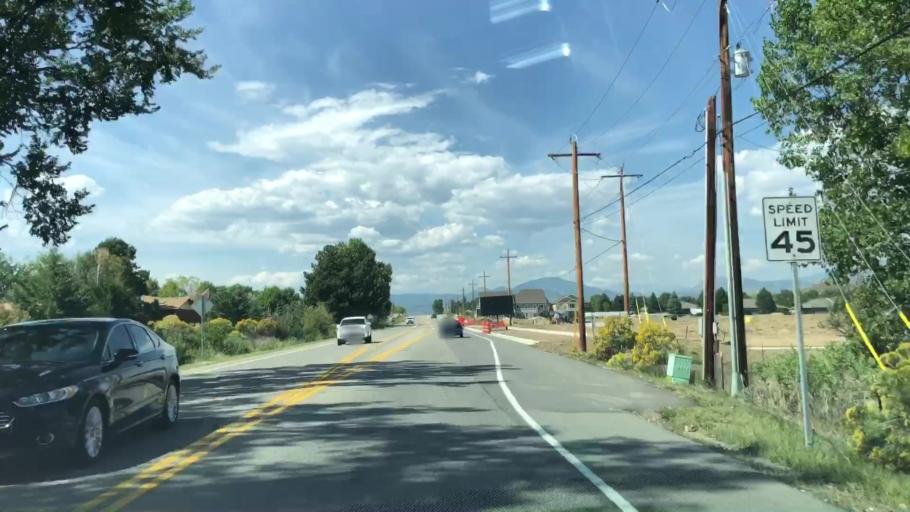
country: US
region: Colorado
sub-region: Larimer County
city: Loveland
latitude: 40.3929
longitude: -105.1260
